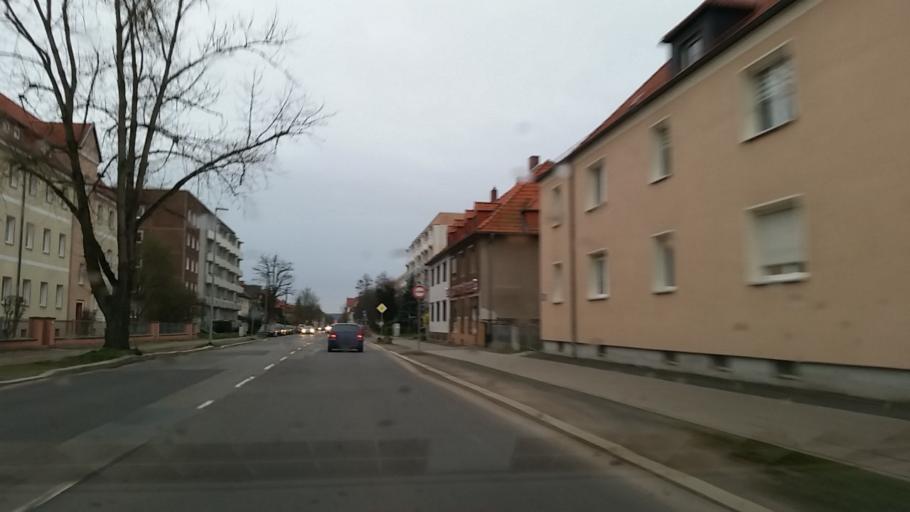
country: DE
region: Thuringia
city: Nordhausen
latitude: 51.5075
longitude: 10.7805
